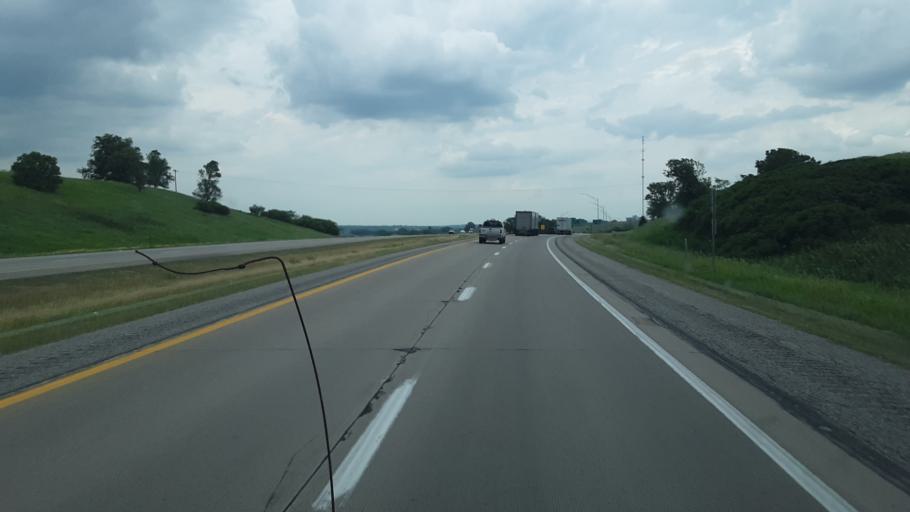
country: US
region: Iowa
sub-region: Pottawattamie County
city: Avoca
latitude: 41.4897
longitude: -95.5864
